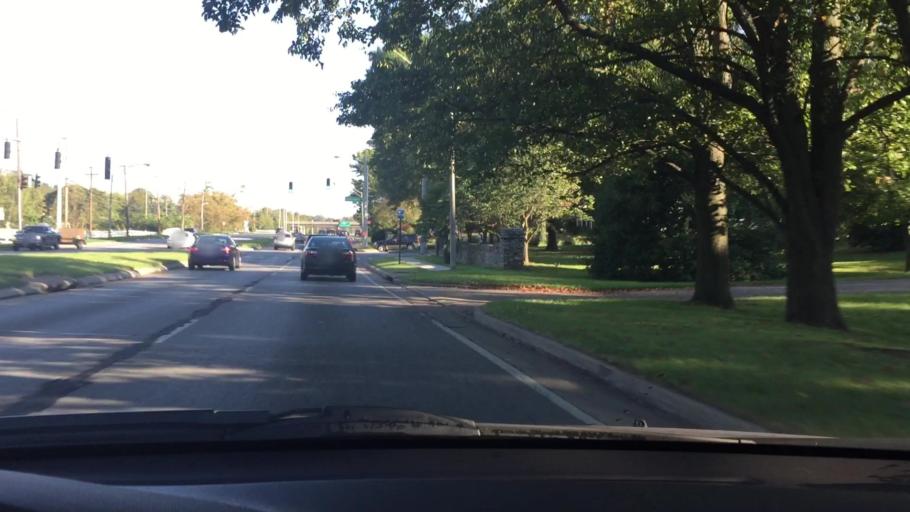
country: US
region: Kentucky
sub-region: Fayette County
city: Lexington
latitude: 37.9870
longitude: -84.4942
